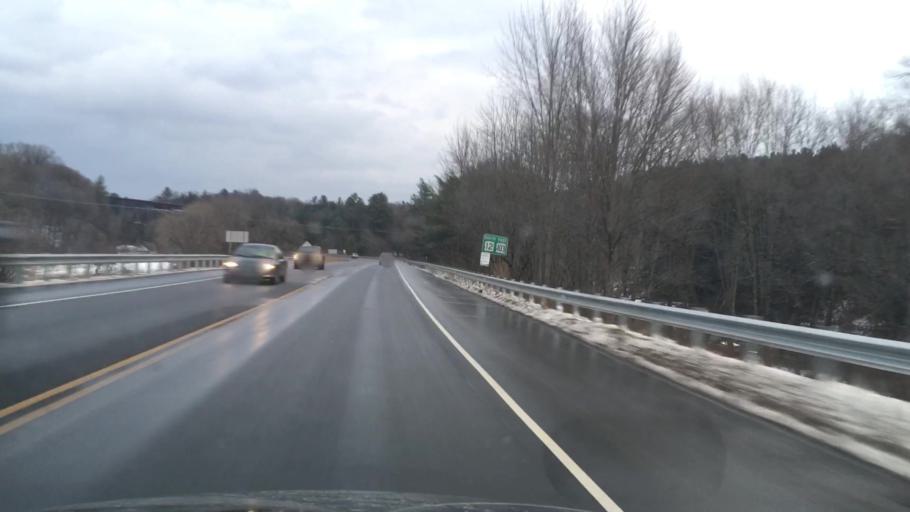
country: US
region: New Hampshire
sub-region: Sullivan County
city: Claremont
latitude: 43.3978
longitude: -72.3920
